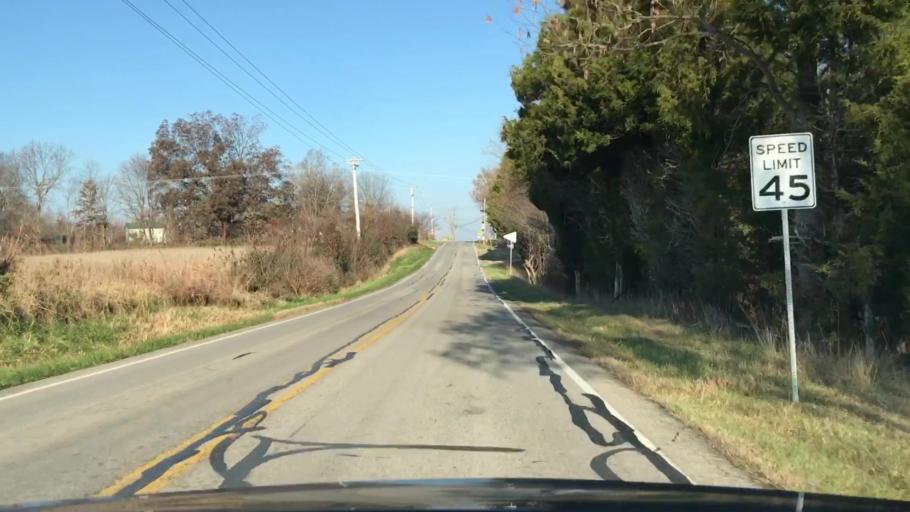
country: US
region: Kentucky
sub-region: Edmonson County
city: Brownsville
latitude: 37.2562
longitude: -86.2817
